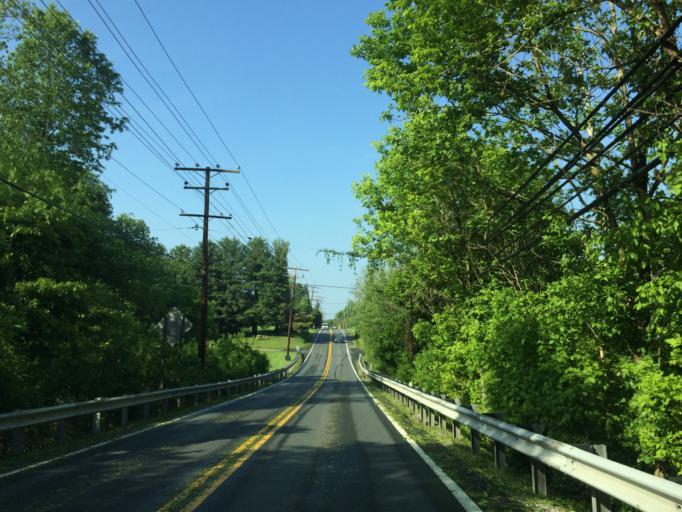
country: US
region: Maryland
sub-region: Howard County
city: Highland
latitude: 39.1871
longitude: -76.9511
